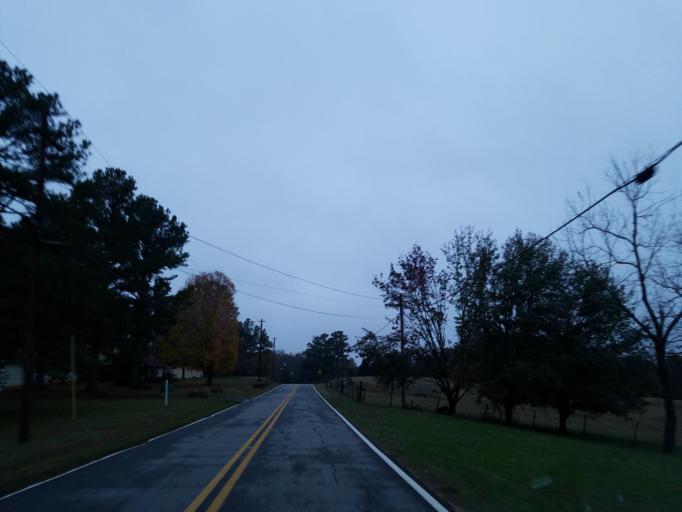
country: US
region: Georgia
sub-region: Cherokee County
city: Ball Ground
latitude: 34.3555
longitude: -84.3759
